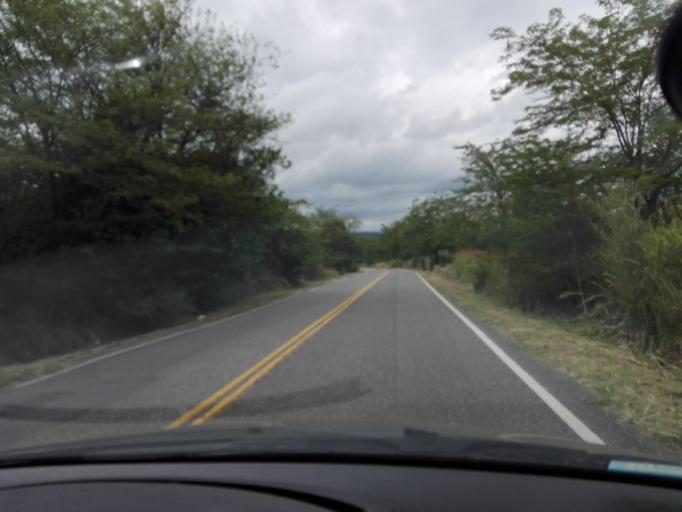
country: AR
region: Cordoba
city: Cuesta Blanca
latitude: -31.5930
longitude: -64.5652
